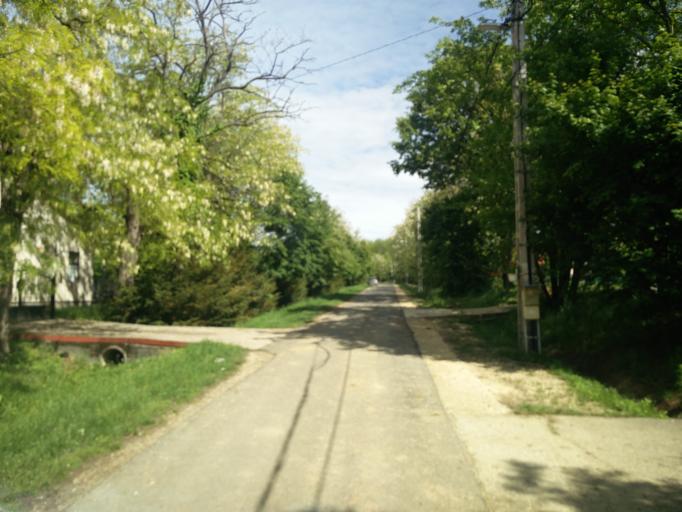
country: HU
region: Tolna
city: Szentgalpuszta
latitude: 46.2823
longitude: 18.6366
